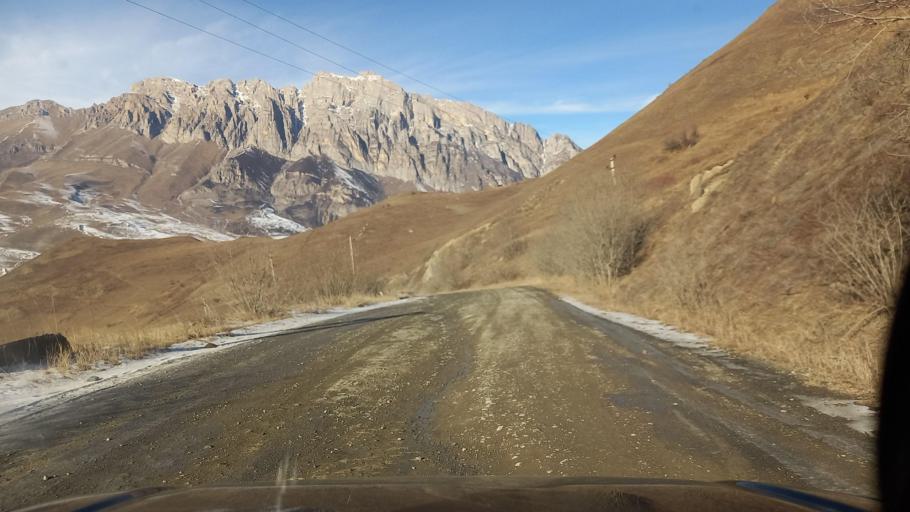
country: RU
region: North Ossetia
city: Verkhniy Fiagdon
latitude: 42.8366
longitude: 44.4680
